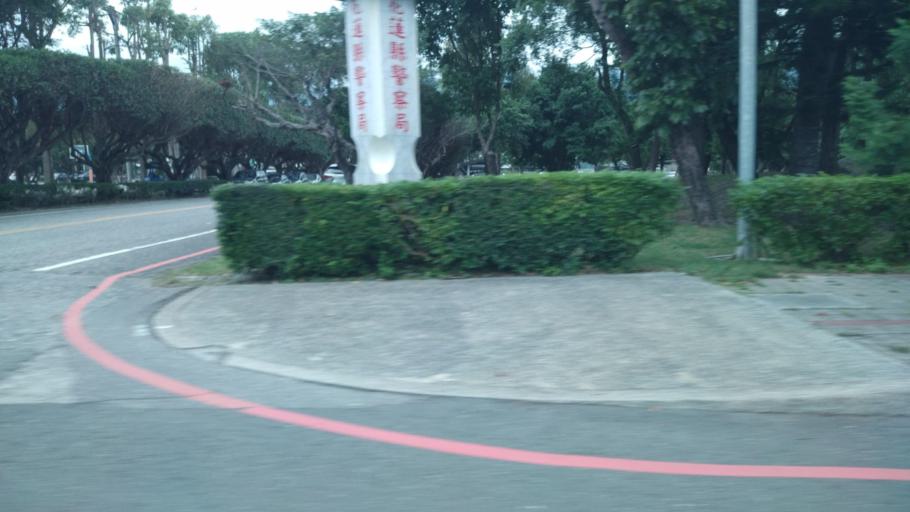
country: TW
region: Taiwan
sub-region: Hualien
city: Hualian
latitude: 23.9931
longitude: 121.6220
